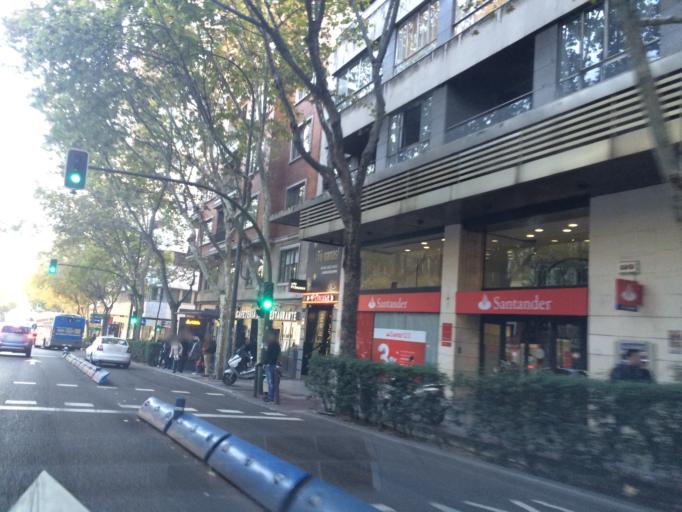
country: ES
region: Madrid
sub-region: Provincia de Madrid
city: Chamberi
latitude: 40.4284
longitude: -3.7148
